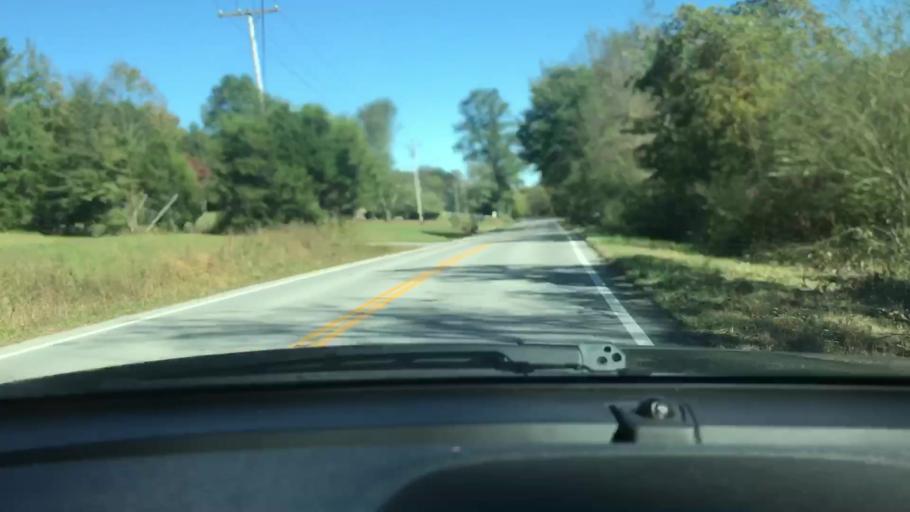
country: US
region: Tennessee
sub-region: Dickson County
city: Charlotte
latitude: 36.1807
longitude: -87.3282
